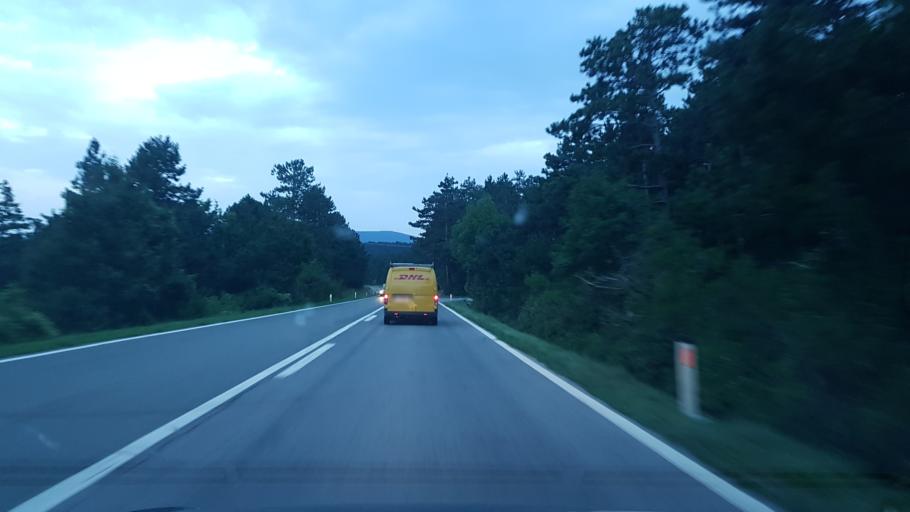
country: SI
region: Divaca
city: Divaca
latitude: 45.6937
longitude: 13.9849
